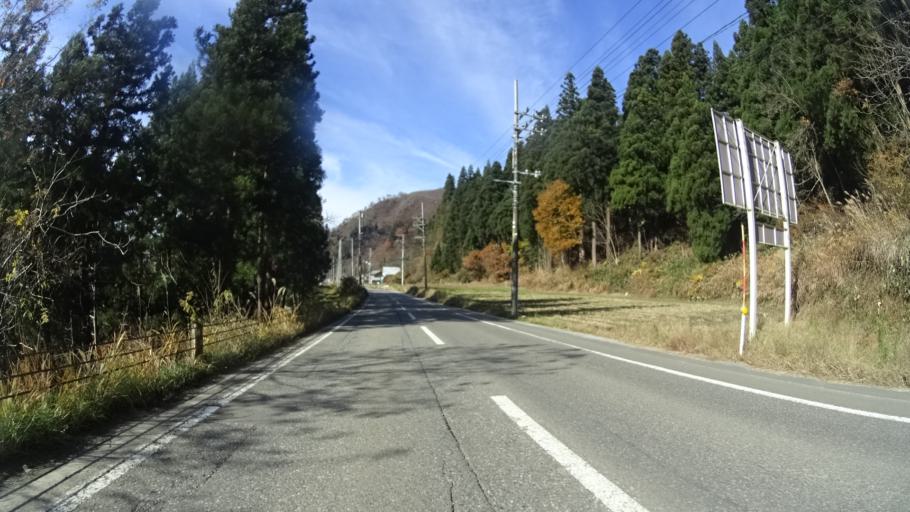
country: JP
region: Niigata
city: Muikamachi
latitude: 37.2223
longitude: 139.0266
